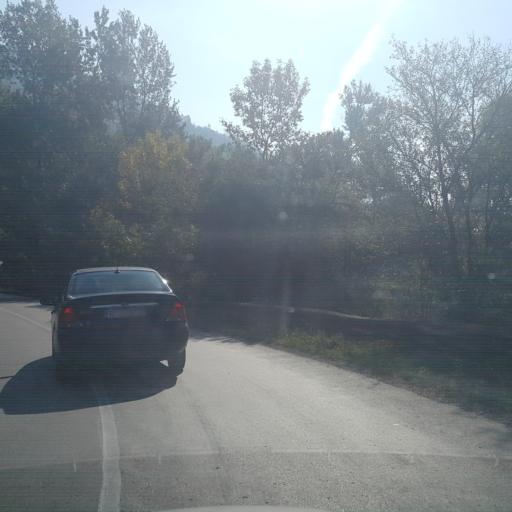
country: RS
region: Central Serbia
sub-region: Pirotski Okrug
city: Pirot
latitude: 43.1899
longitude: 22.5676
